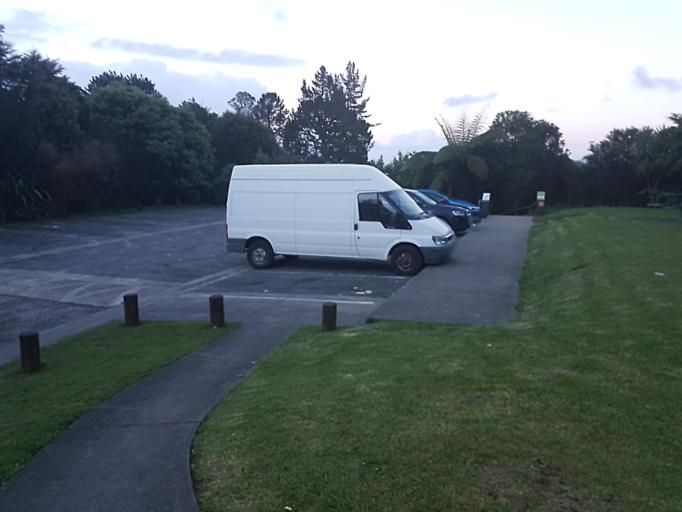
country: NZ
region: Bay of Plenty
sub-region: Tauranga City
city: Tauranga
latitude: -37.7607
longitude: 176.2416
